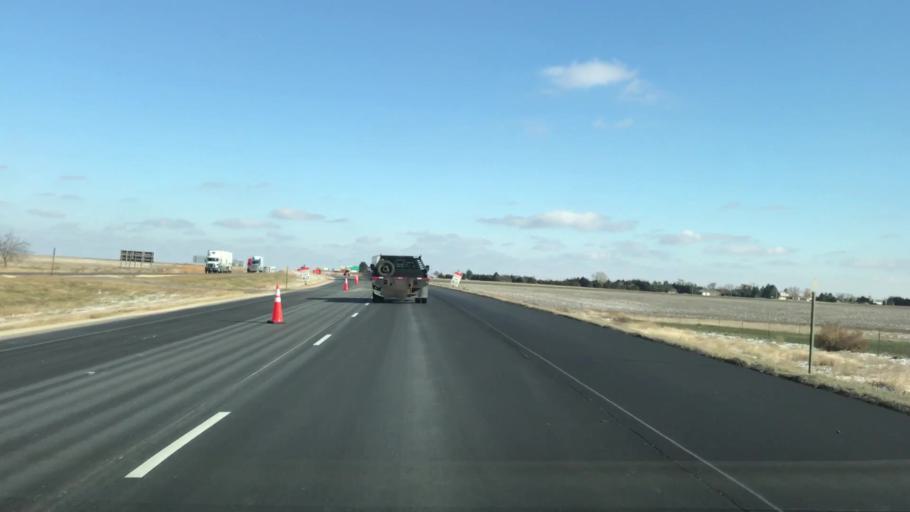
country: US
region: Kansas
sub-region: Ellis County
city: Hays
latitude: 38.8782
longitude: -99.2699
